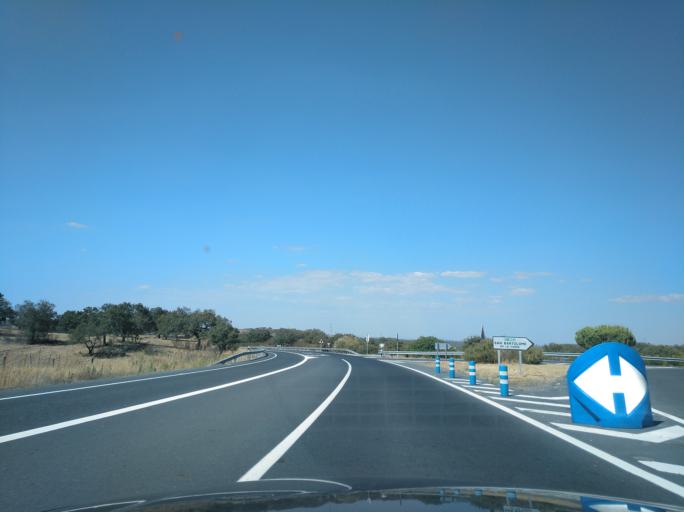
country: ES
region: Andalusia
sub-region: Provincia de Huelva
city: San Bartolome de la Torre
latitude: 37.4650
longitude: -7.1231
